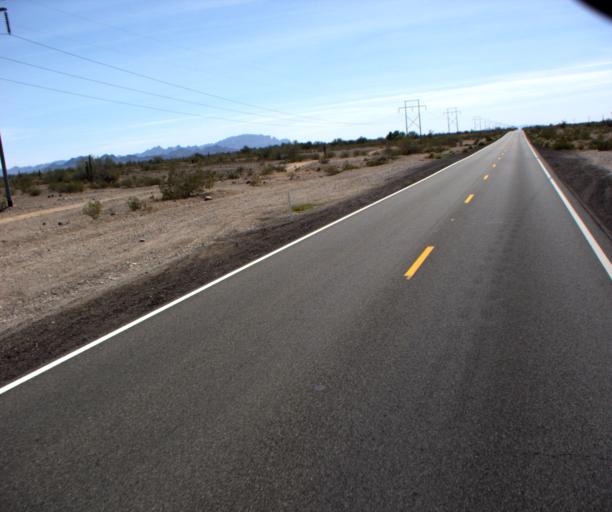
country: US
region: Arizona
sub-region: La Paz County
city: Quartzsite
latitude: 33.6036
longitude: -114.2171
